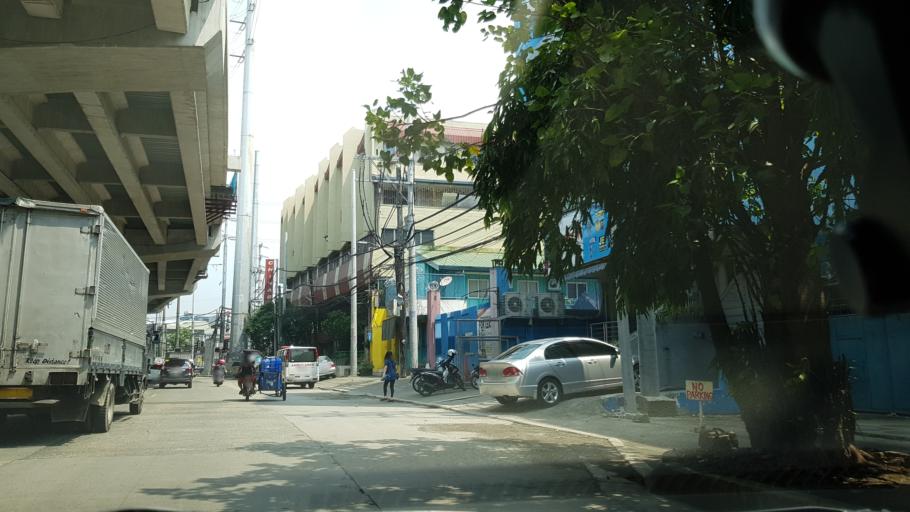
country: PH
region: Metro Manila
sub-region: San Juan
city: San Juan
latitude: 14.6144
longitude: 121.0170
